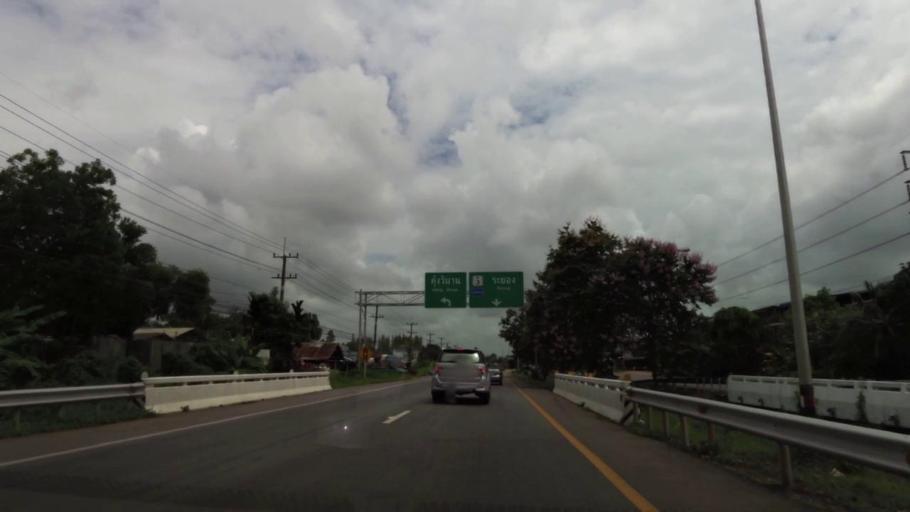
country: TH
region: Chanthaburi
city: Na Yai Am
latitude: 12.7592
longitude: 101.8578
